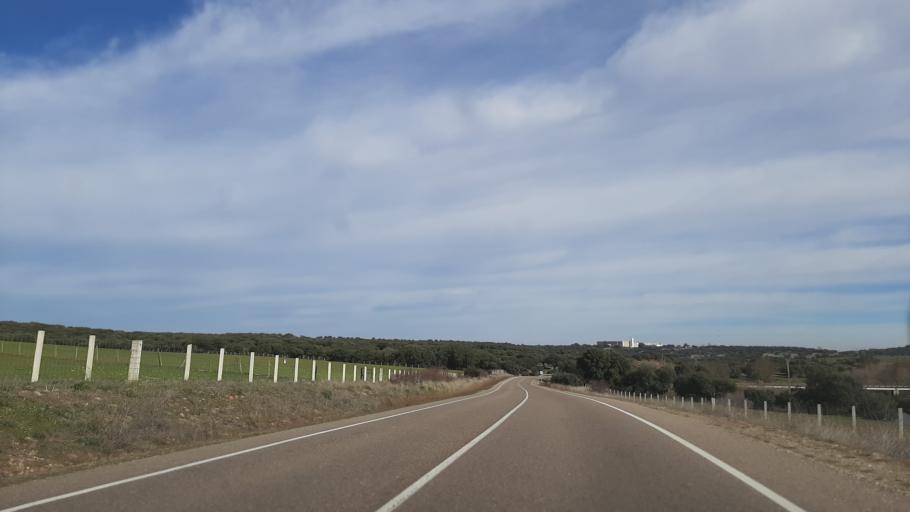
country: ES
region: Castille and Leon
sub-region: Provincia de Salamanca
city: Anover de Tormes
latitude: 41.0890
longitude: -5.9146
